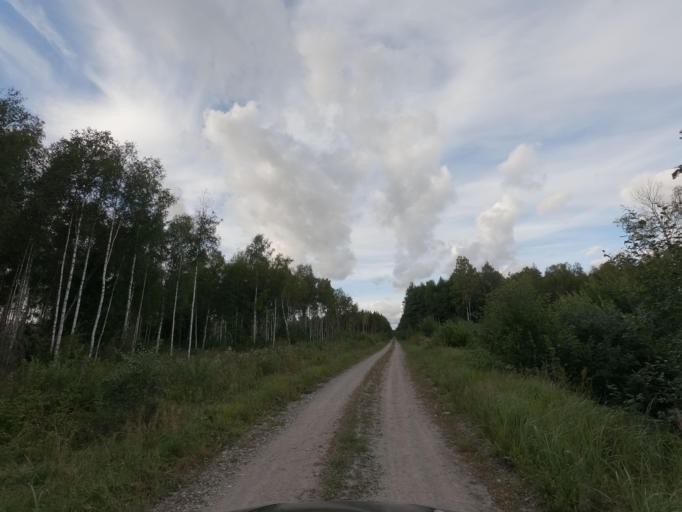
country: EE
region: Raplamaa
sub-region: Rapla vald
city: Rapla
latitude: 59.0054
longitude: 24.7572
